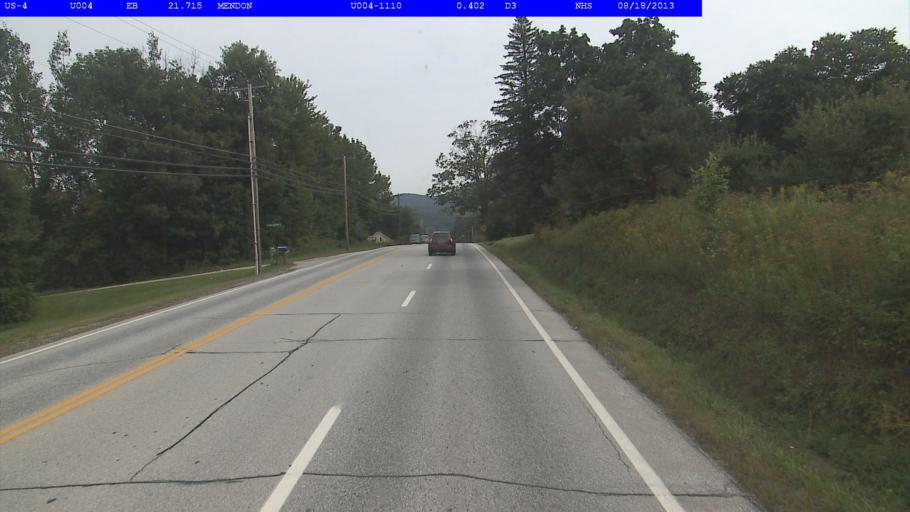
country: US
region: Vermont
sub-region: Rutland County
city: Rutland
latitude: 43.6397
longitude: -72.9330
